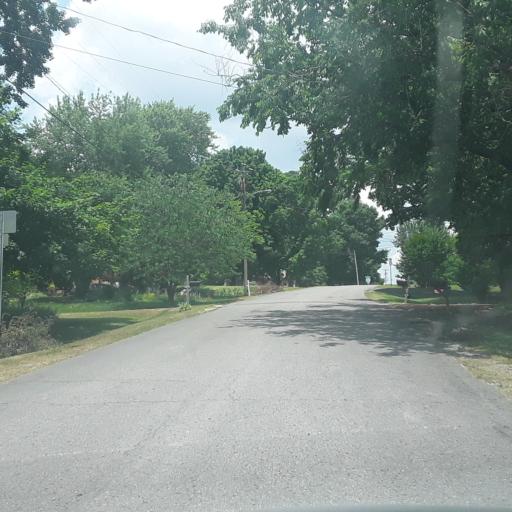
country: US
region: Tennessee
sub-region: Williamson County
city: Brentwood Estates
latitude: 36.0593
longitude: -86.7114
